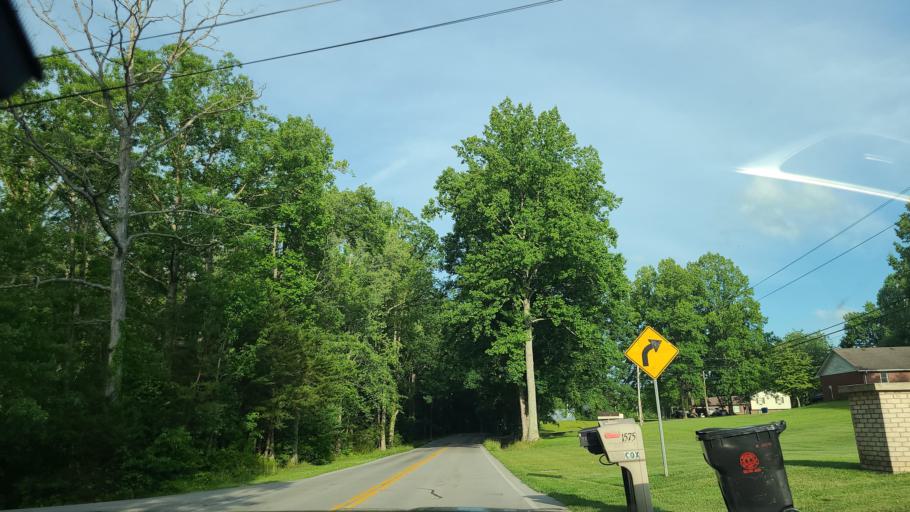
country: US
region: Kentucky
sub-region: Whitley County
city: Corbin
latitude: 36.8920
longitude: -84.2228
